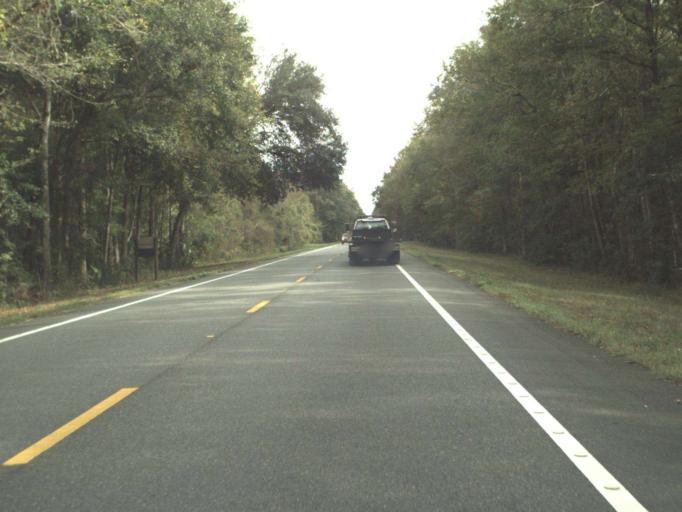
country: US
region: Florida
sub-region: Leon County
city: Woodville
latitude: 30.1553
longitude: -83.9928
